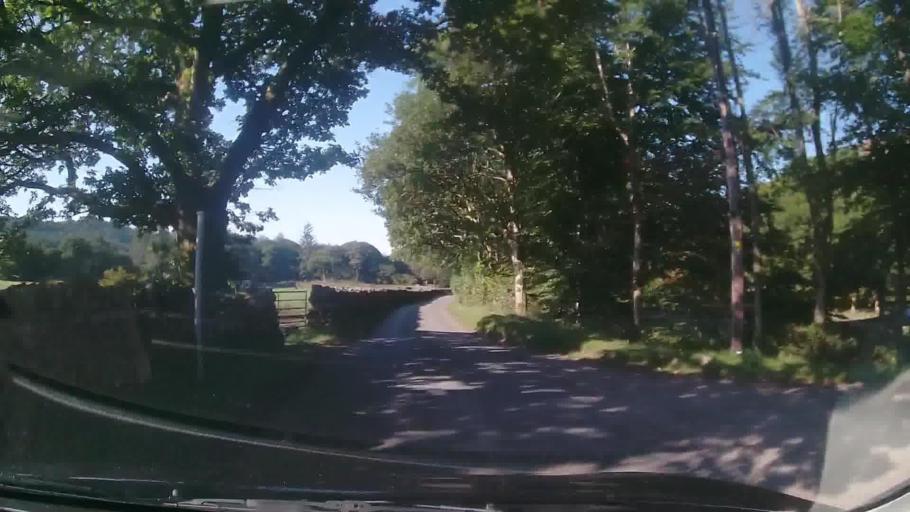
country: GB
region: England
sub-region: Cumbria
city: Millom
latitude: 54.3951
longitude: -3.2744
